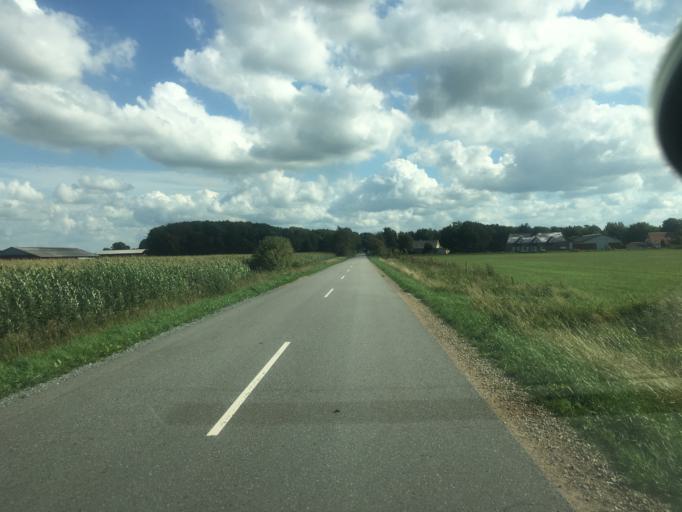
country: DE
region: Schleswig-Holstein
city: Ellhoft
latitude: 54.9519
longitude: 8.9625
